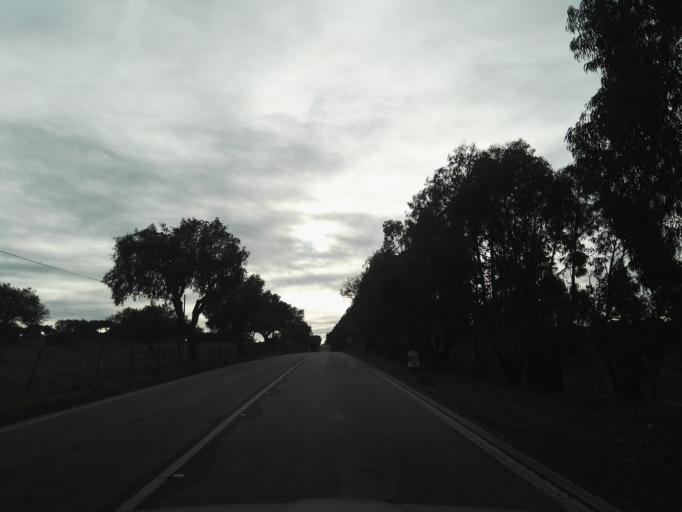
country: PT
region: Evora
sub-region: Redondo
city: Redondo
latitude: 38.6643
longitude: -7.5241
